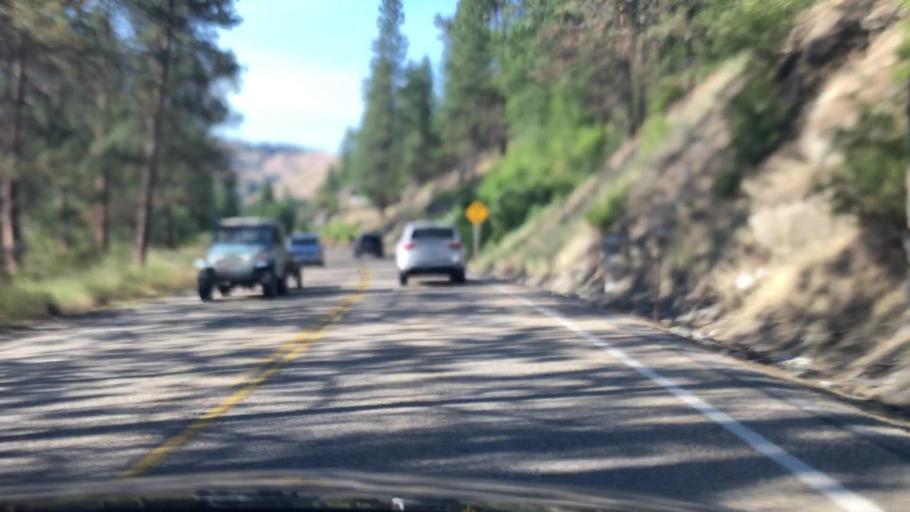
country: US
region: Idaho
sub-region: Boise County
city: Idaho City
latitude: 44.0651
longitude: -116.1209
